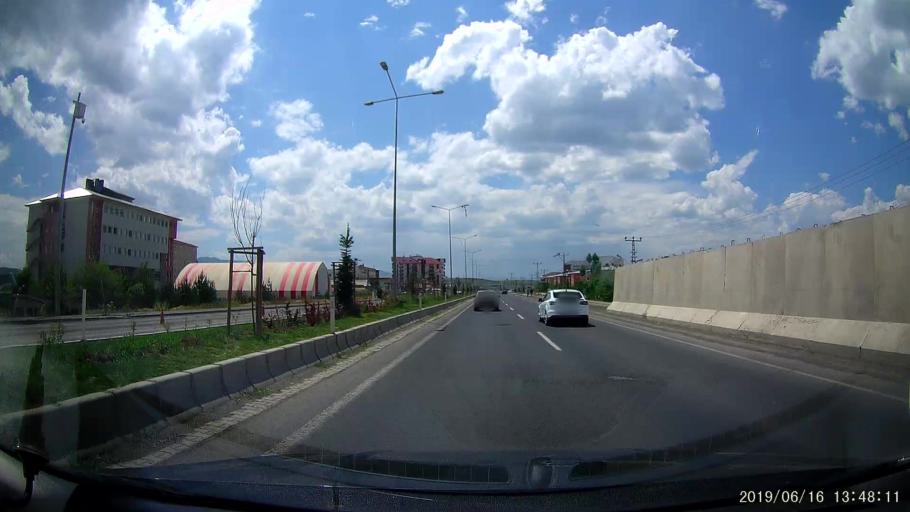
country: TR
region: Agri
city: Agri
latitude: 39.7144
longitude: 43.0119
